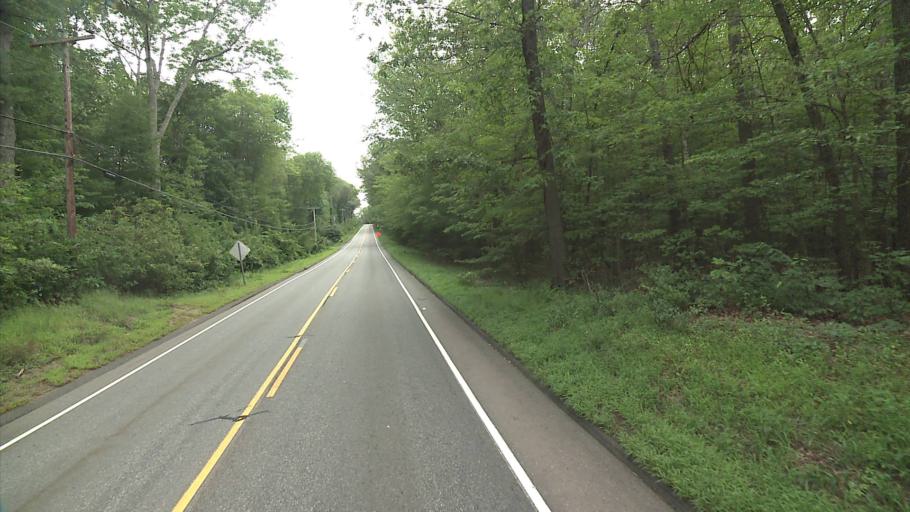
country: US
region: Connecticut
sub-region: Tolland County
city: Storrs
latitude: 41.8740
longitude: -72.2315
